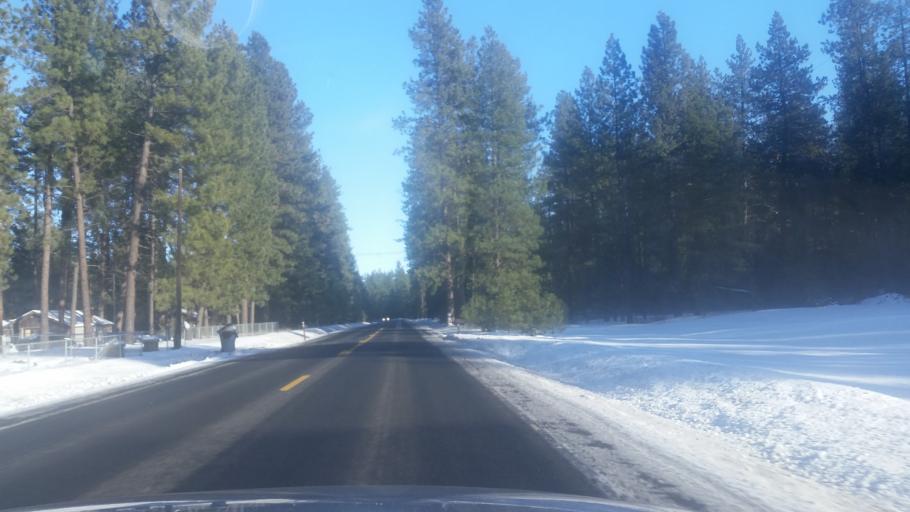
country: US
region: Washington
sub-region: Spokane County
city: Spokane
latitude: 47.5708
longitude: -117.4779
